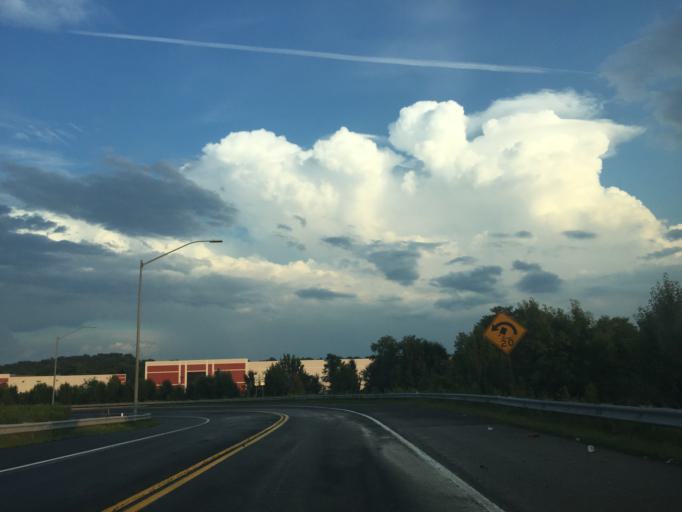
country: US
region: Maryland
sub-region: Harford County
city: Riverside
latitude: 39.4704
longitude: -76.2339
